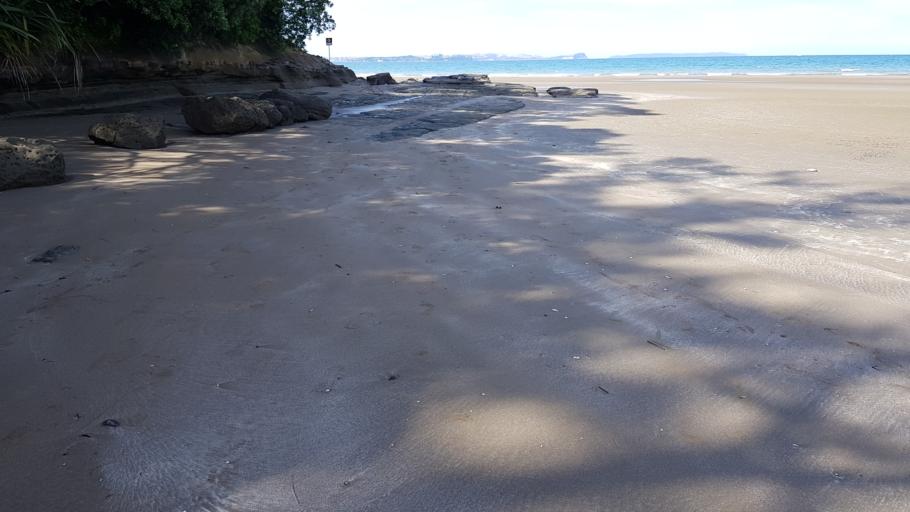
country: NZ
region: Auckland
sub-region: Auckland
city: Rothesay Bay
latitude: -36.6791
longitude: 174.7482
